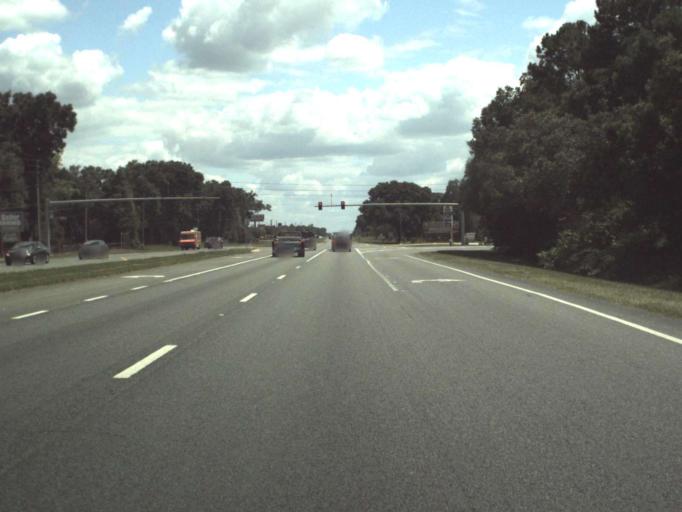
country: US
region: Florida
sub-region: Marion County
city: Ocala
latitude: 29.2680
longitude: -82.1521
